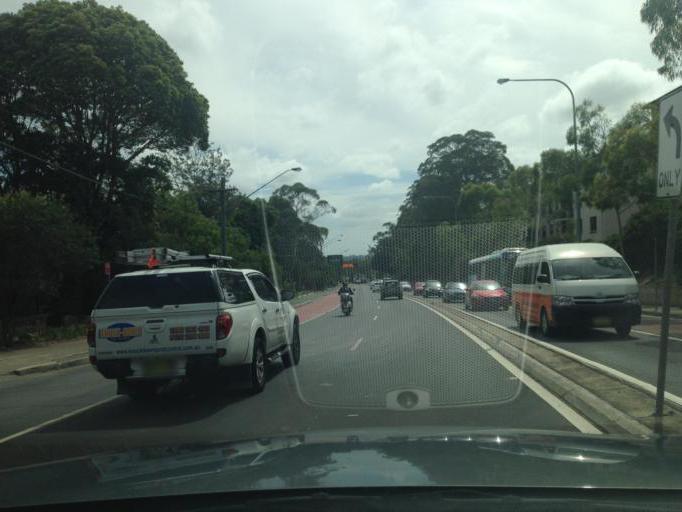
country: AU
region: New South Wales
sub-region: Lane Cove
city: Lane Cove
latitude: -33.8117
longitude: 151.1682
